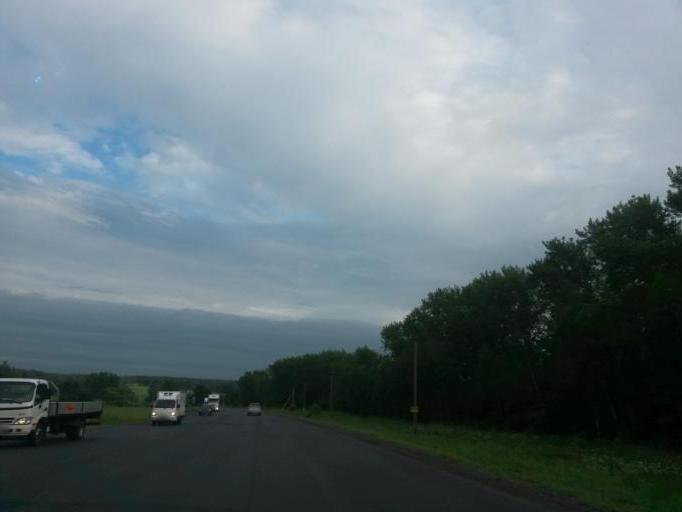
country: RU
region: Moskovskaya
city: Barybino
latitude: 55.2575
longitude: 37.8324
